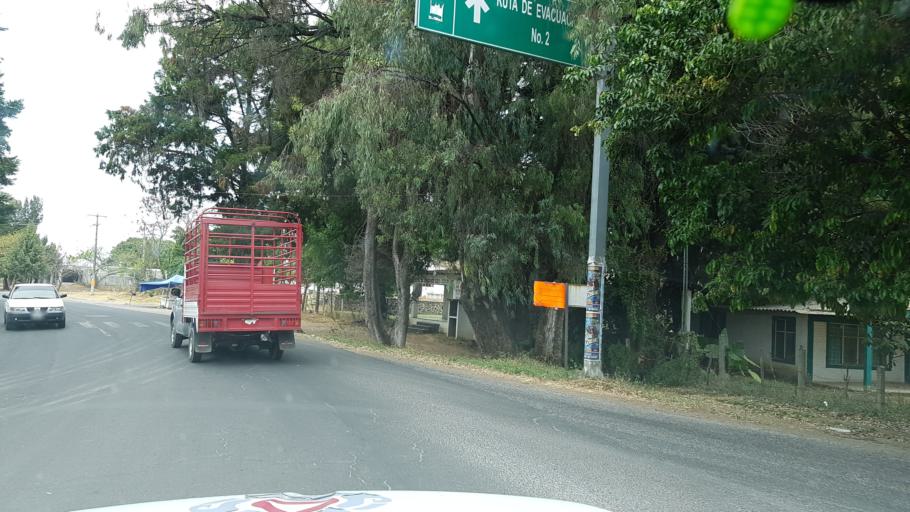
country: MX
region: Morelos
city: Ocuituco
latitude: 18.8801
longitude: -98.7823
